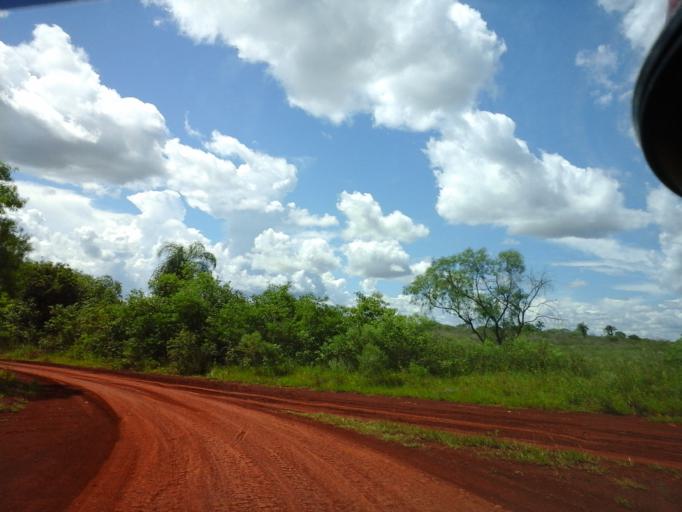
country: AR
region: Misiones
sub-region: Departamento de Apostoles
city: Apostoles
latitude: -27.9759
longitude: -55.7732
